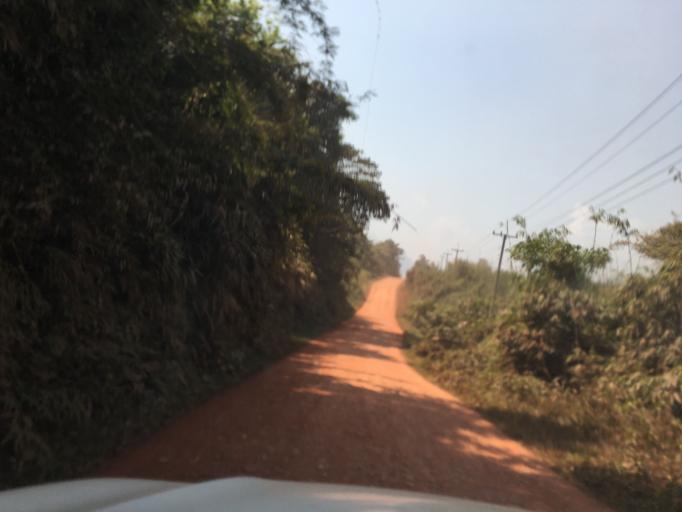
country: LA
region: Bolikhamxai
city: Bolikhan
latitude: 18.7504
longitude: 103.6061
